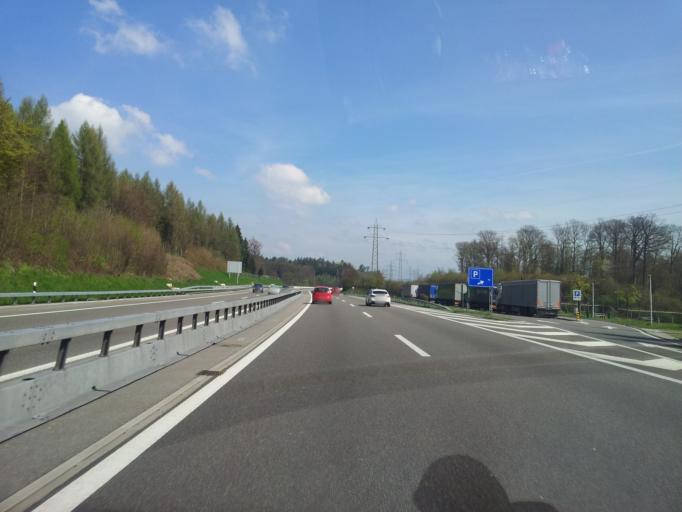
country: CH
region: Aargau
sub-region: Bezirk Lenzburg
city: Othmarsingen
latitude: 47.4013
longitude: 8.2061
